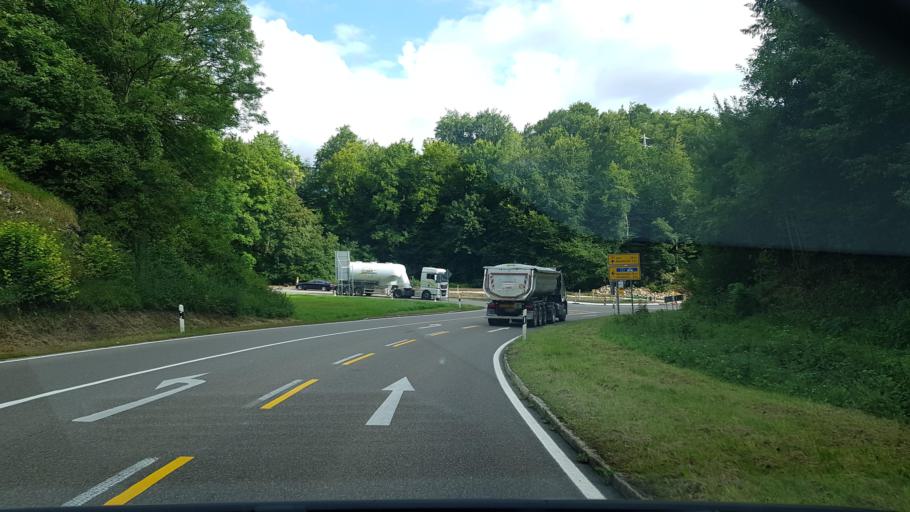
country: DE
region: Baden-Wuerttemberg
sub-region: Tuebingen Region
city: Blaubeuren
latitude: 48.4272
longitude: 9.7684
